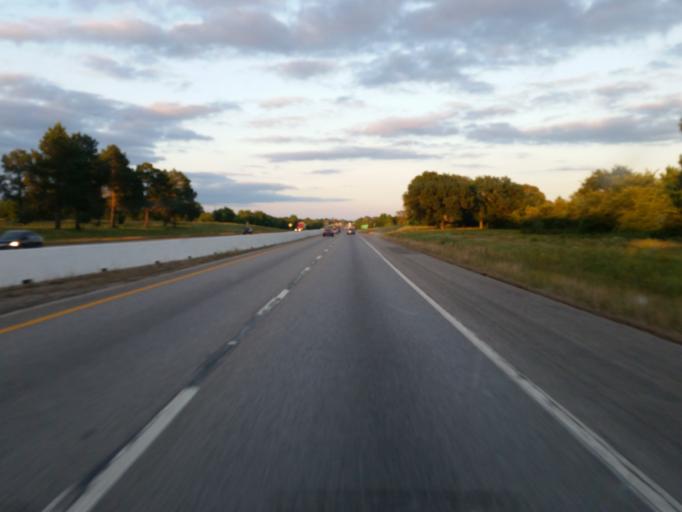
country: US
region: Texas
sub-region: Van Zandt County
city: Van
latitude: 32.5001
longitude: -95.6108
